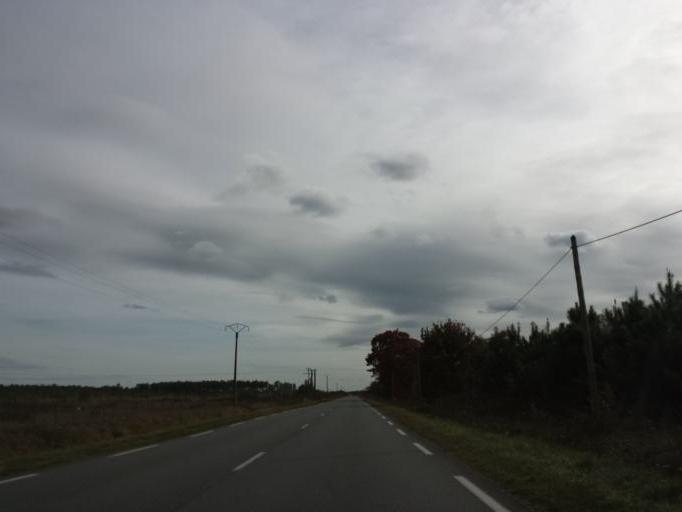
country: FR
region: Aquitaine
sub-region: Departement de la Gironde
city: Marcheprime
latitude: 44.7667
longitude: -0.9242
